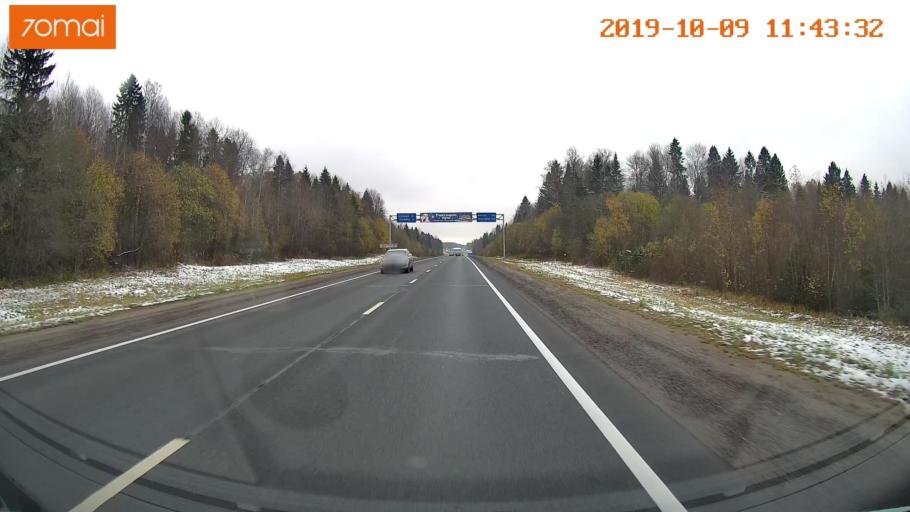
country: RU
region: Vologda
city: Gryazovets
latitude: 58.8956
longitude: 40.1860
